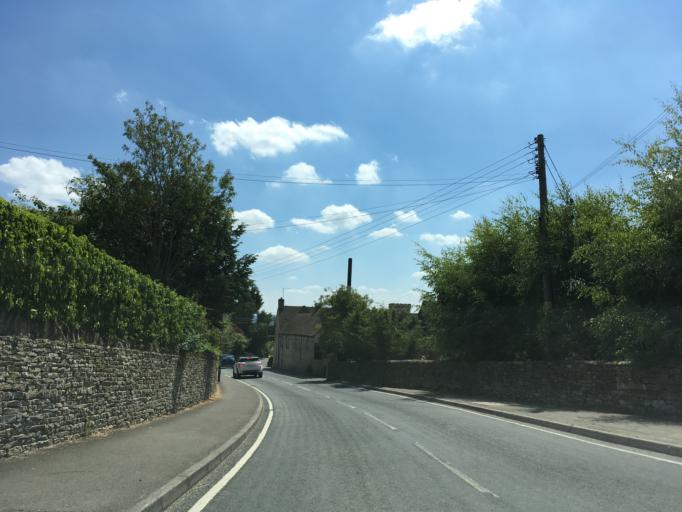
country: GB
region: England
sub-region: Gloucestershire
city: Stroud
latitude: 51.7615
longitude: -2.2329
